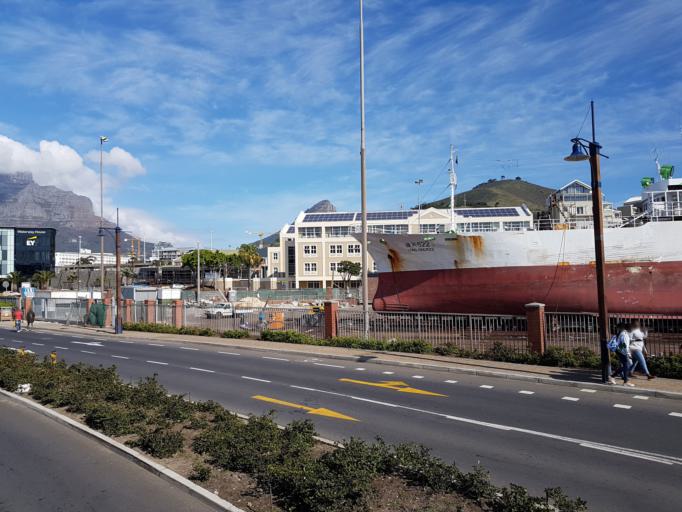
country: ZA
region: Western Cape
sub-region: City of Cape Town
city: Cape Town
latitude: -33.9104
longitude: 18.4228
